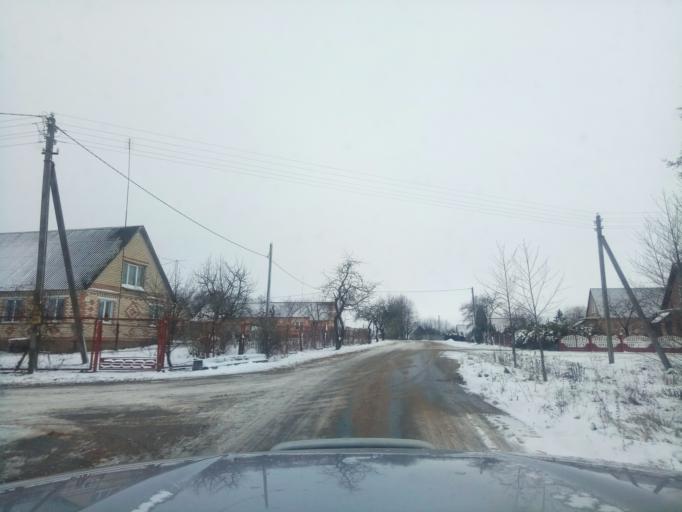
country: BY
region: Minsk
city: Kapyl'
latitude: 53.1634
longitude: 27.0881
